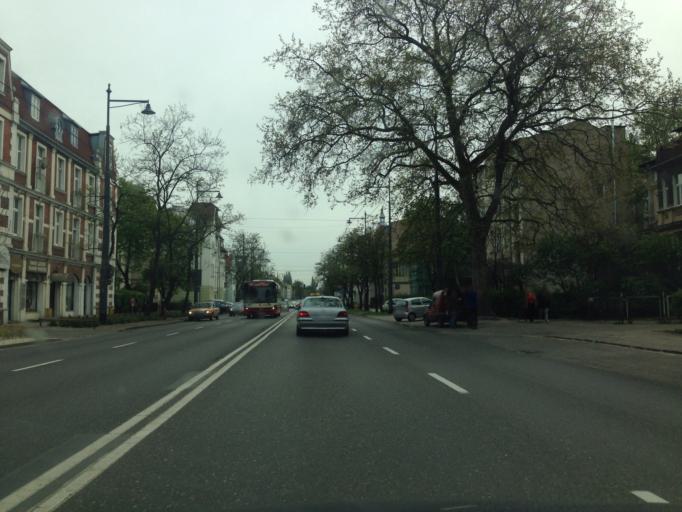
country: PL
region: Pomeranian Voivodeship
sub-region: Sopot
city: Sopot
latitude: 54.4374
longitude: 18.5609
